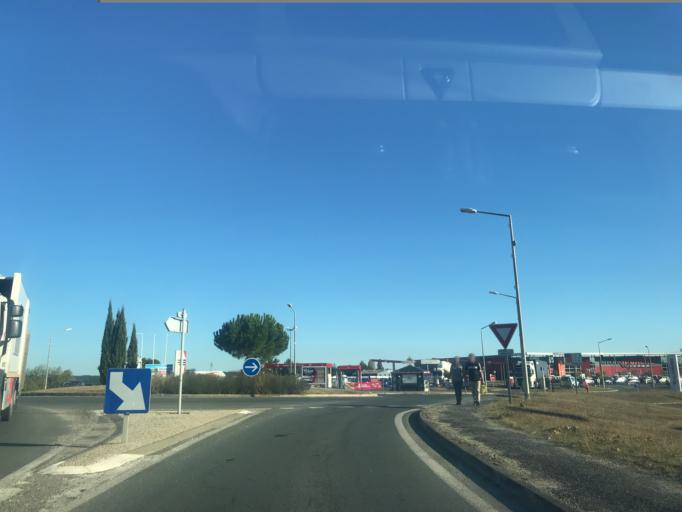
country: FR
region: Poitou-Charentes
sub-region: Departement de la Charente-Maritime
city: Montguyon
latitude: 45.2126
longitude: -0.1771
